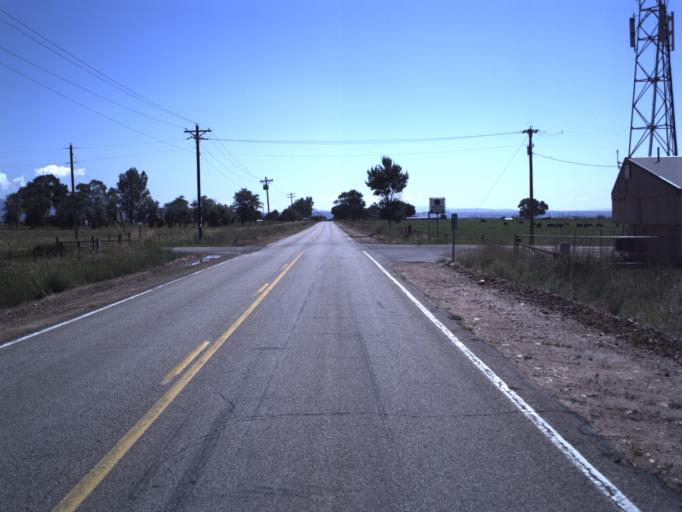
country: US
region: Utah
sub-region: Duchesne County
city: Roosevelt
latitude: 40.4329
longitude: -110.0119
